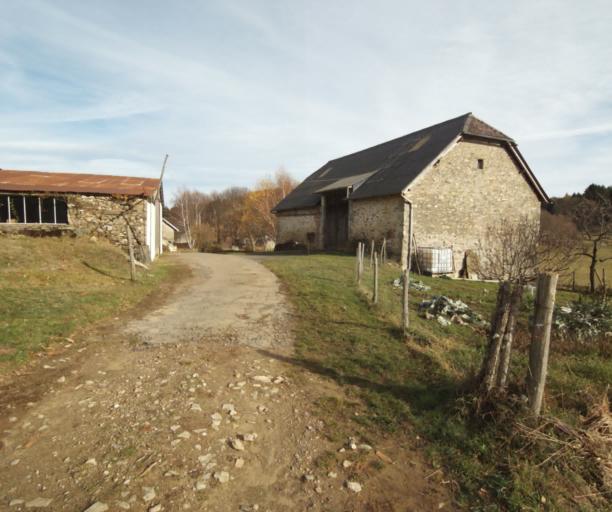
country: FR
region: Limousin
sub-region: Departement de la Correze
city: Sainte-Fortunade
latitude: 45.1850
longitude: 1.7377
